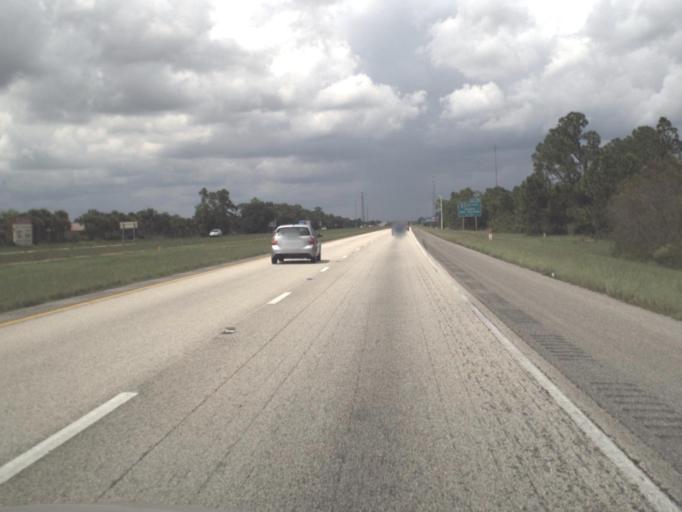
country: US
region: Florida
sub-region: Charlotte County
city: Harbour Heights
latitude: 27.0073
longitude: -82.0403
